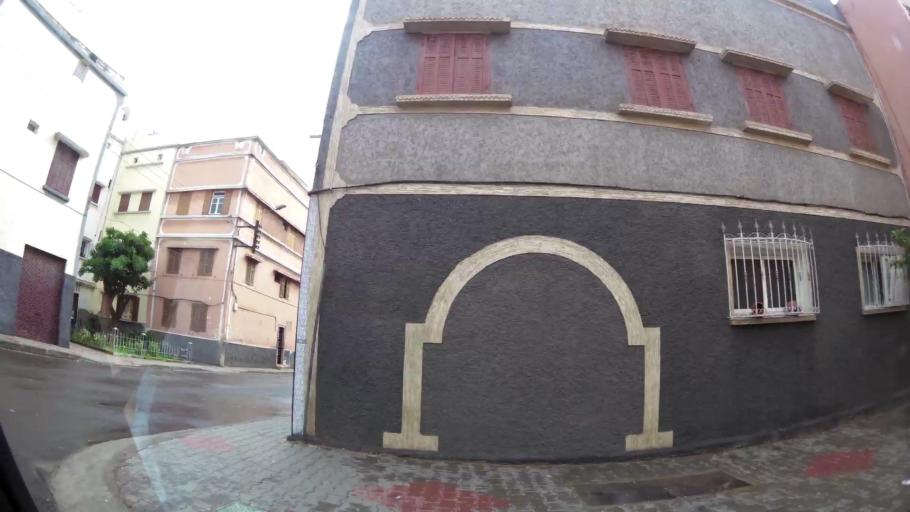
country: MA
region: Grand Casablanca
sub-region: Casablanca
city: Casablanca
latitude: 33.5443
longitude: -7.5781
